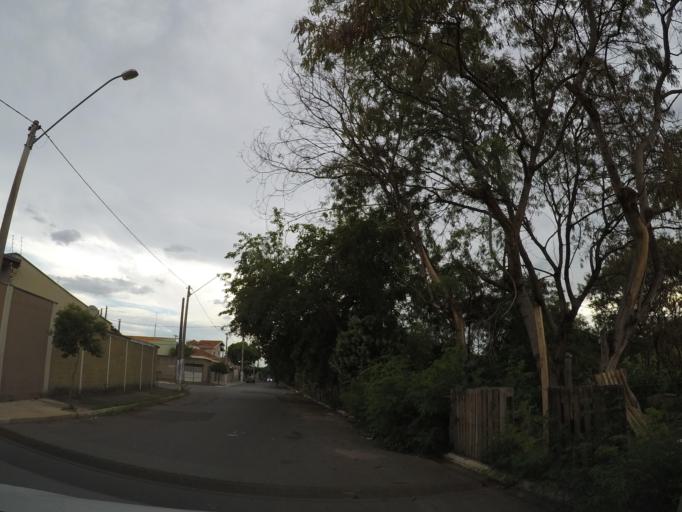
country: BR
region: Sao Paulo
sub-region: Sumare
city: Sumare
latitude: -22.8122
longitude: -47.2547
